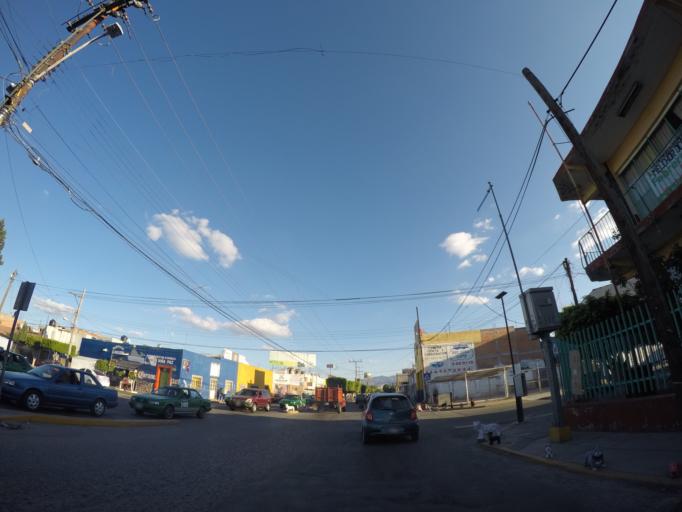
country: MX
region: San Luis Potosi
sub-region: San Luis Potosi
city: San Luis Potosi
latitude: 22.1673
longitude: -100.9807
